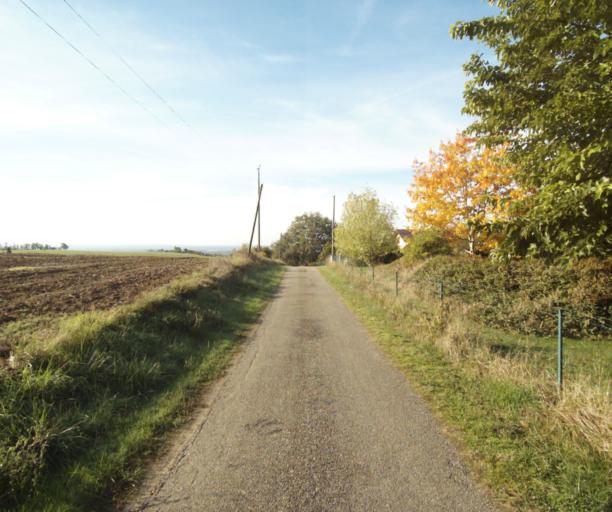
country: FR
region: Midi-Pyrenees
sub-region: Departement du Tarn-et-Garonne
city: Nohic
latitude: 43.9090
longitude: 1.4621
